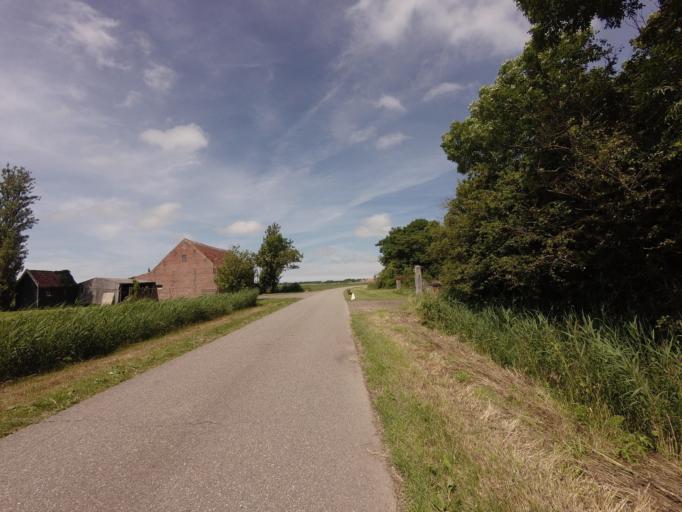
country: NL
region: North Holland
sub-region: Gemeente Texel
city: Den Burg
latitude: 53.0762
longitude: 4.8816
